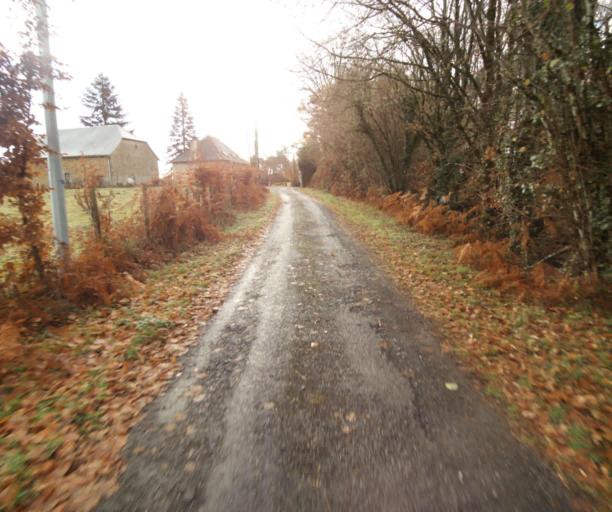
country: FR
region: Limousin
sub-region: Departement de la Correze
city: Saint-Mexant
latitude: 45.2494
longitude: 1.6478
